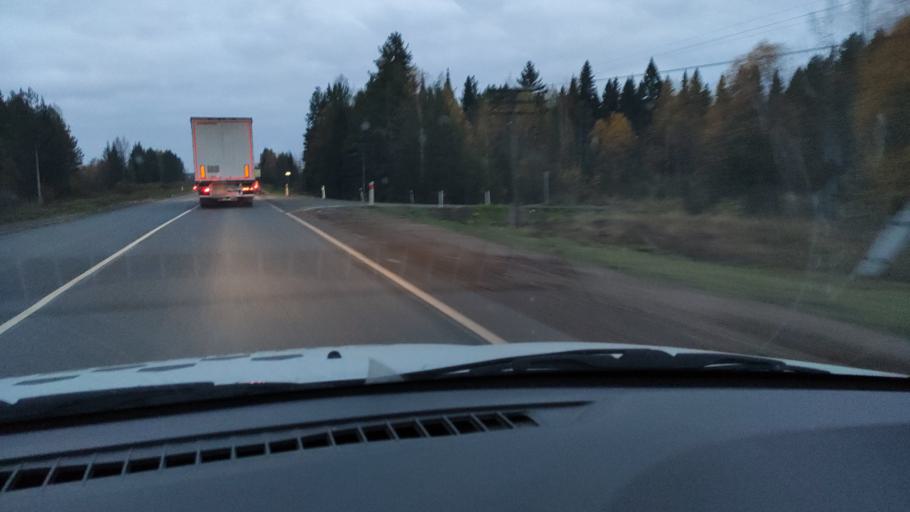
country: RU
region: Kirov
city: Kostino
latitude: 58.8382
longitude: 53.3036
